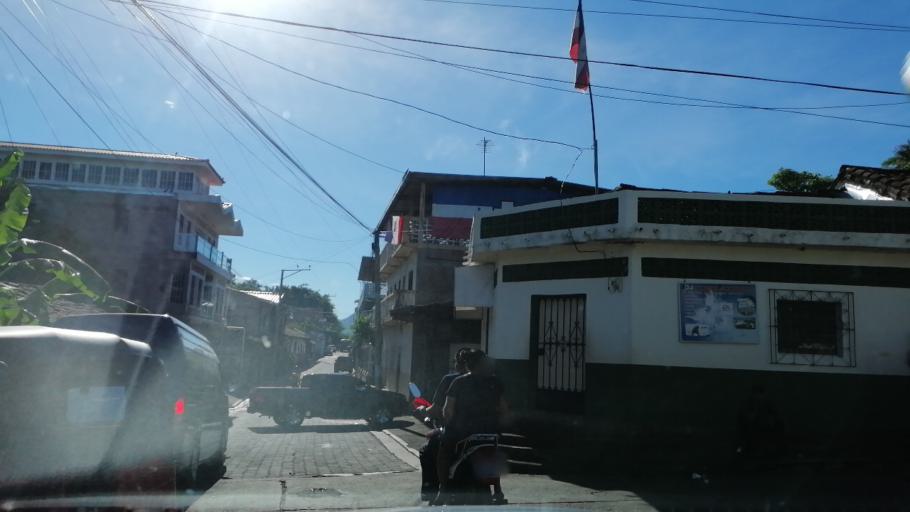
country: SV
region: Morazan
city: Cacaopera
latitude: 13.7720
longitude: -88.0769
